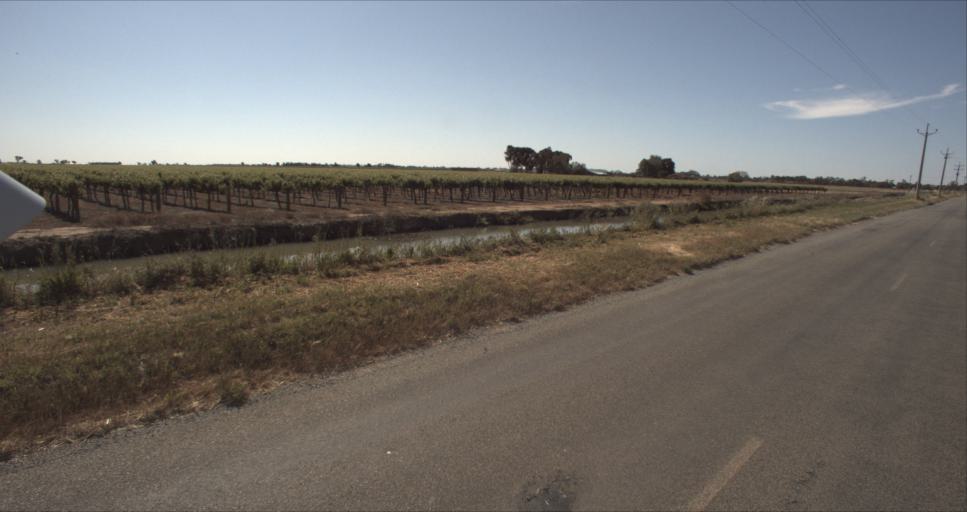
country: AU
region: New South Wales
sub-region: Leeton
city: Leeton
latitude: -34.5797
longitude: 146.3801
